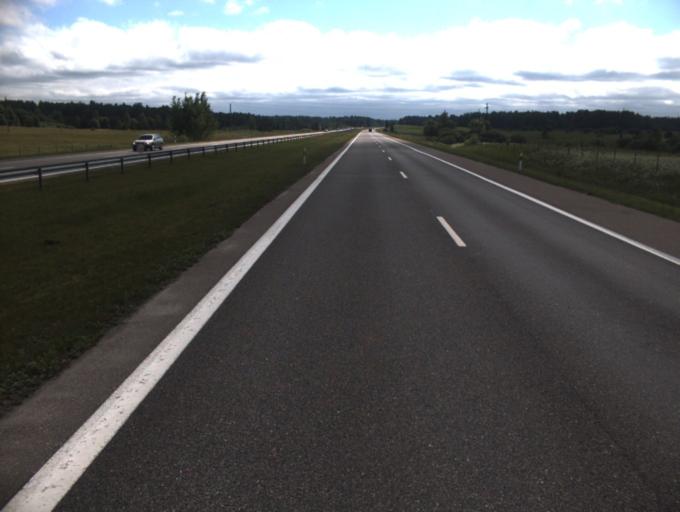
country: LT
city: Rietavas
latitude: 55.6622
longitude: 21.7549
